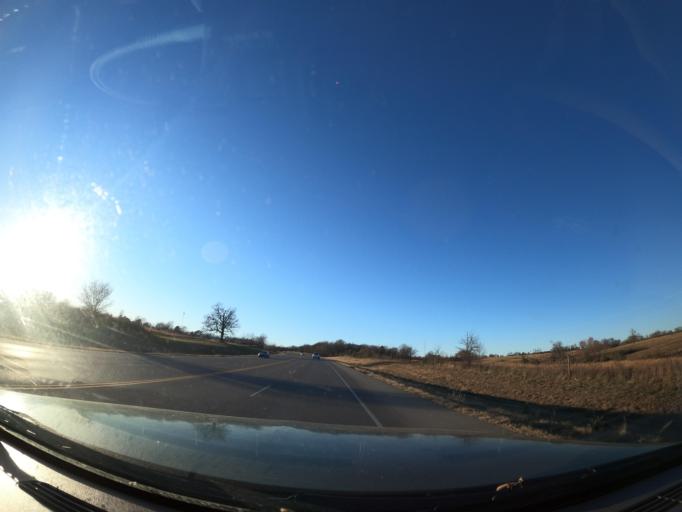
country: US
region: Oklahoma
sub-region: Pittsburg County
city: Hartshorne
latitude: 34.8932
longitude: -95.6256
